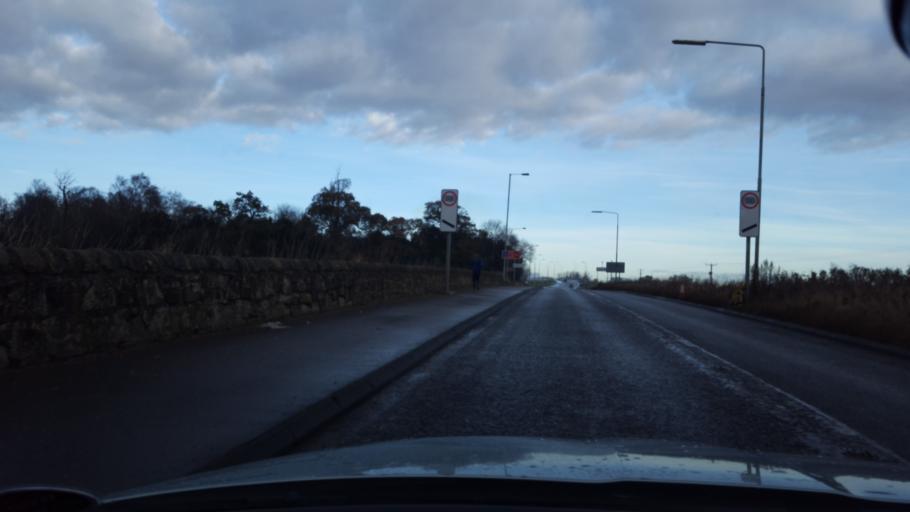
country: GB
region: Scotland
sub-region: Edinburgh
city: Queensferry
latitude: 55.9757
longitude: -3.3981
